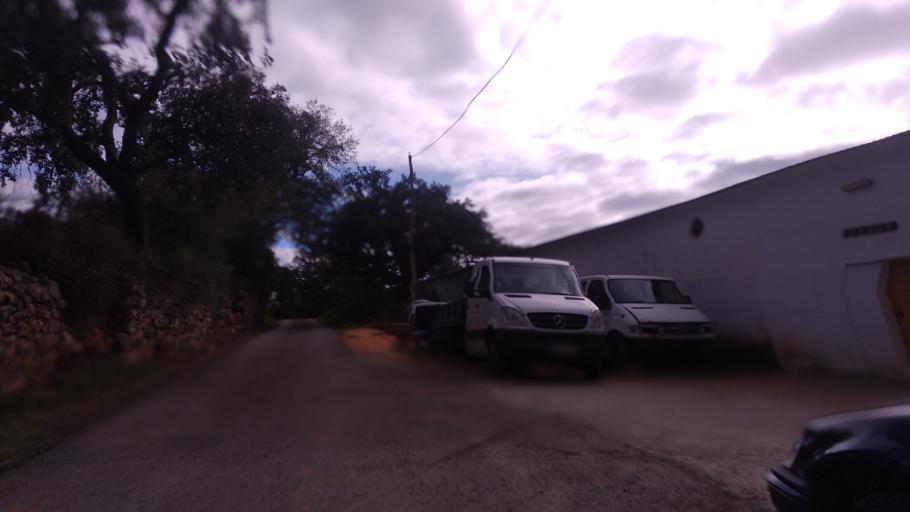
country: PT
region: Faro
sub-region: Loule
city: Almancil
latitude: 37.0993
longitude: -8.0479
